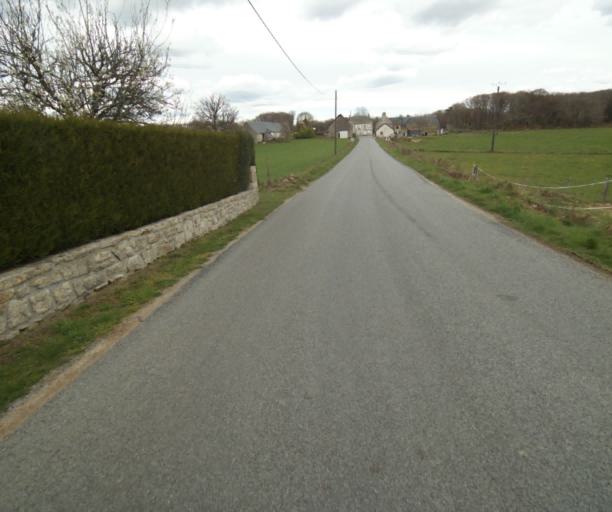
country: FR
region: Limousin
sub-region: Departement de la Correze
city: Argentat
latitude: 45.2113
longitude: 1.9177
